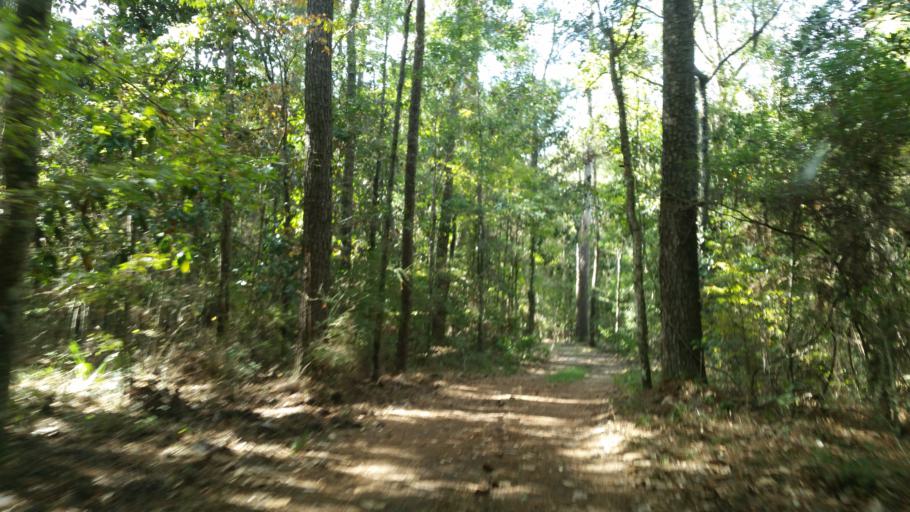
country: US
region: Alabama
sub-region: Baldwin County
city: Spanish Fort
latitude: 30.7375
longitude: -87.9221
